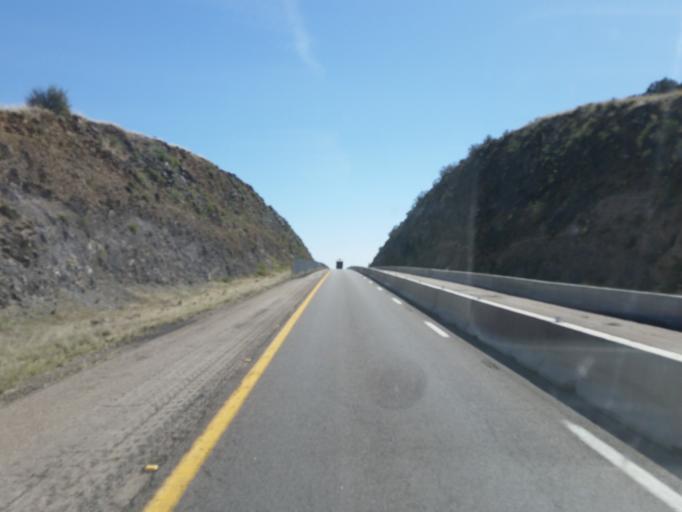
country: US
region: Arizona
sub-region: Mohave County
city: Peach Springs
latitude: 35.2392
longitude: -113.2021
